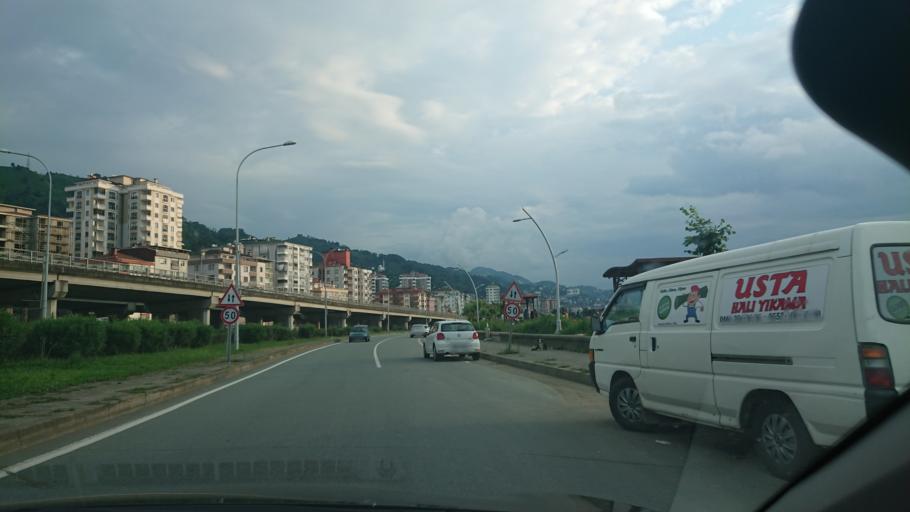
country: TR
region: Rize
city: Gundogdu
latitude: 41.0387
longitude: 40.5651
